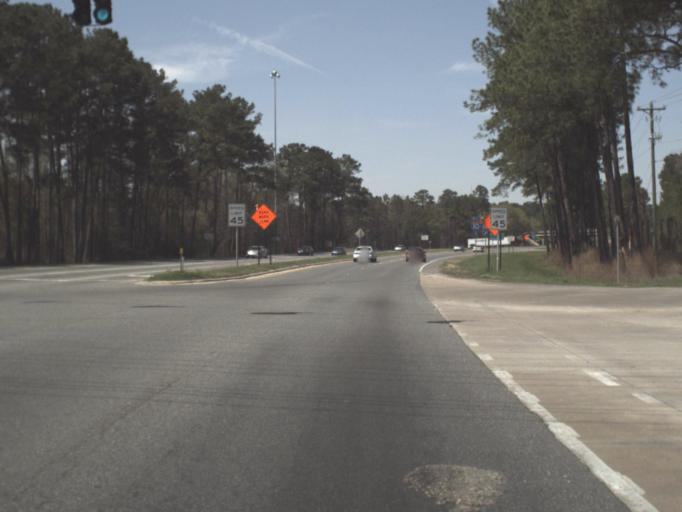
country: US
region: Florida
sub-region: Gadsden County
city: Midway
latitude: 30.4855
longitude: -84.4226
